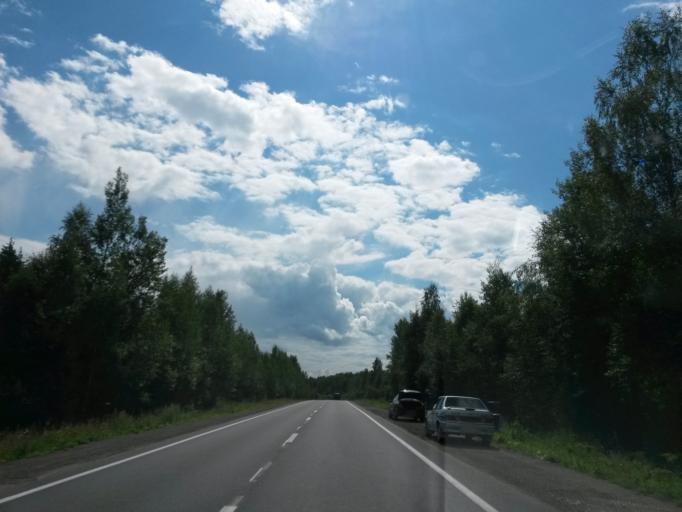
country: RU
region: Jaroslavl
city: Gavrilov-Yam
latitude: 57.2957
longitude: 39.9493
